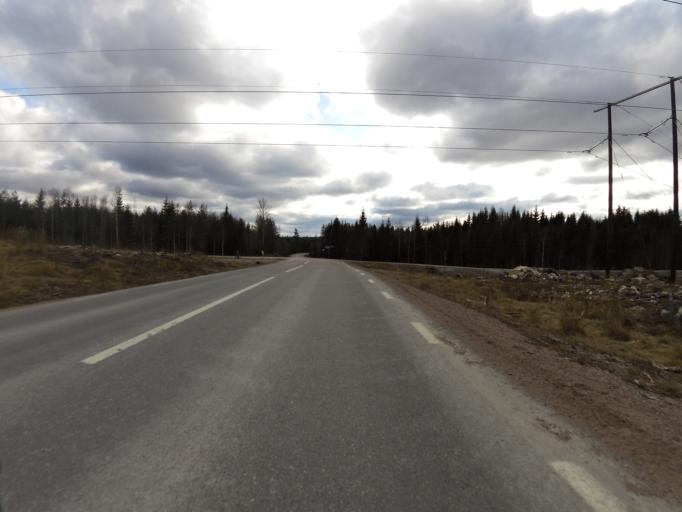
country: SE
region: Dalarna
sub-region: Avesta Kommun
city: Avesta
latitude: 60.3107
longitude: 16.2079
